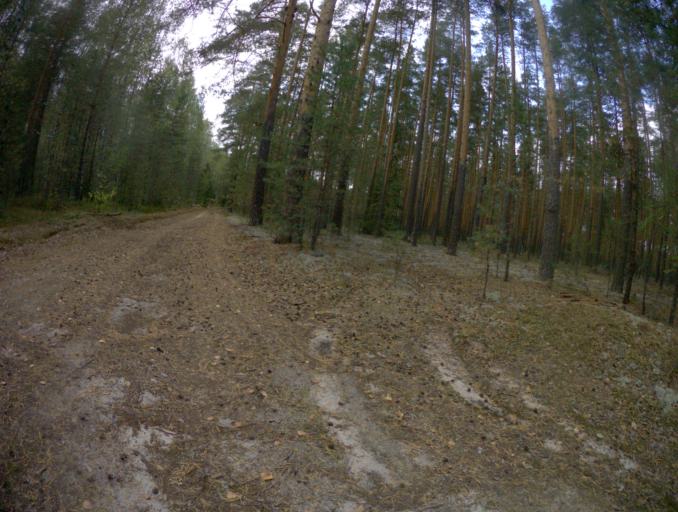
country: RU
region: Vladimir
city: Ivanishchi
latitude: 55.8670
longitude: 40.3973
